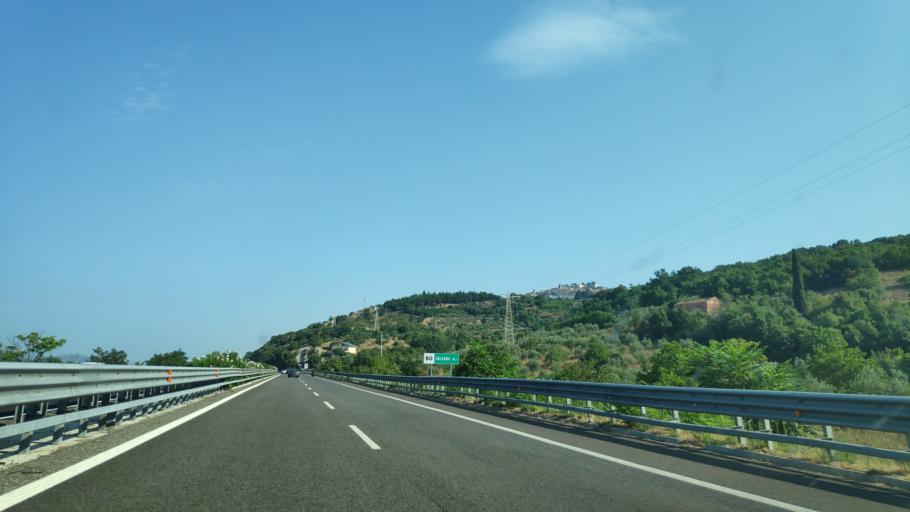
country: IT
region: Campania
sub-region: Provincia di Salerno
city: Atena Lucana
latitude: 40.4428
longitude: 15.5504
